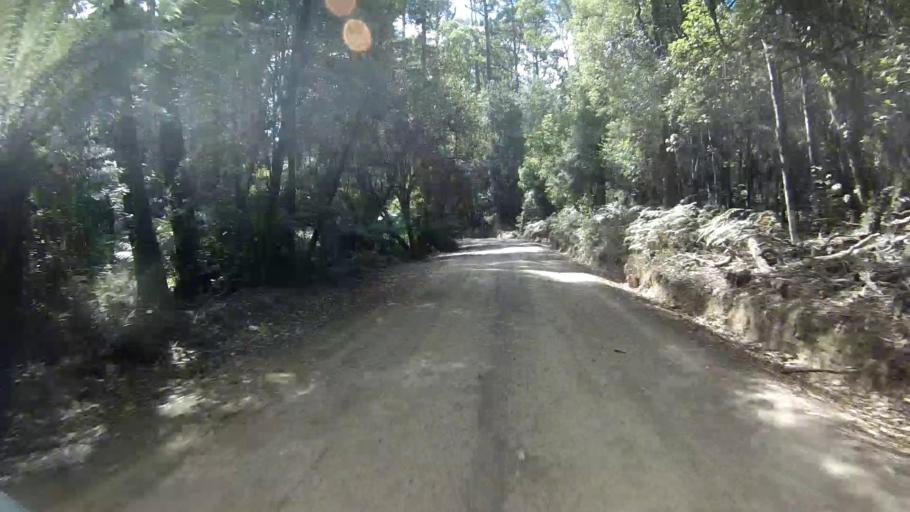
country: AU
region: Tasmania
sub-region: Derwent Valley
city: New Norfolk
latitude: -42.6830
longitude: 146.7082
